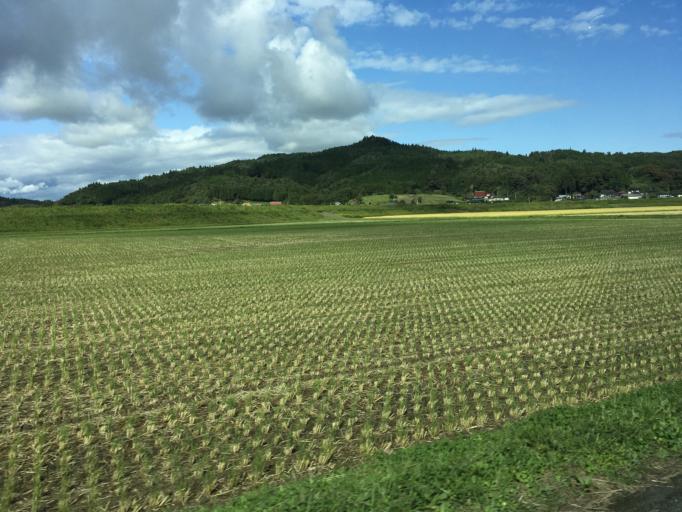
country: JP
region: Iwate
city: Ichinoseki
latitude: 38.8412
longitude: 141.2726
